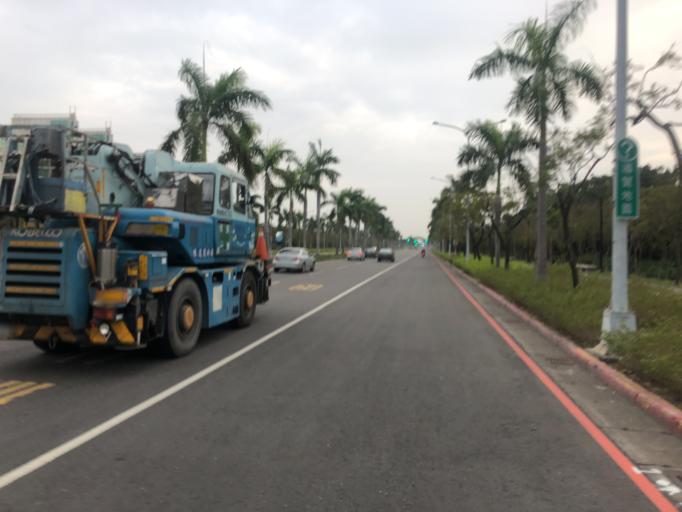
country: TW
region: Taiwan
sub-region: Tainan
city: Tainan
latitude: 23.0986
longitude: 120.2809
